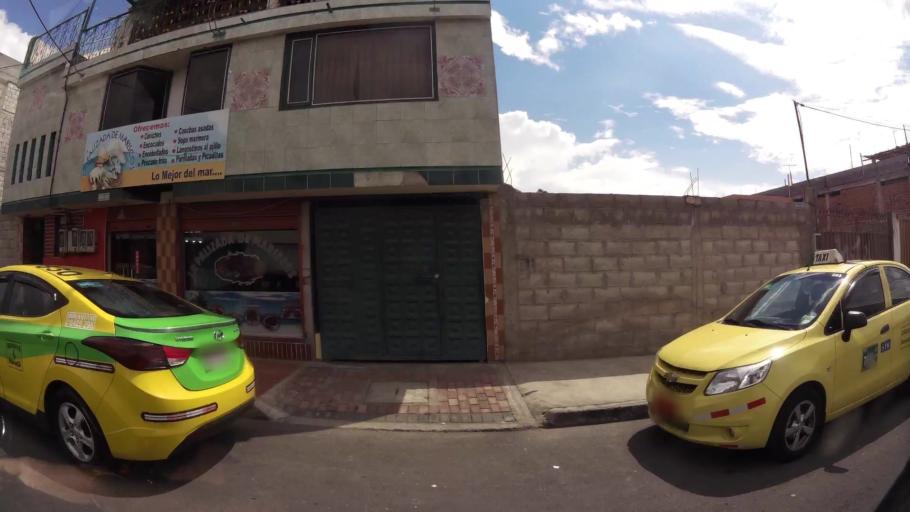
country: EC
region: Pichincha
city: Quito
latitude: -0.0969
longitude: -78.4549
